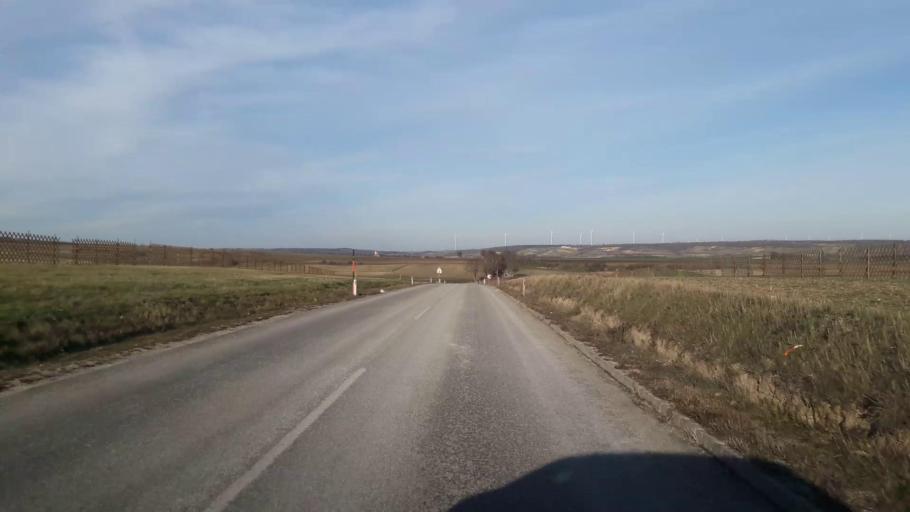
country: AT
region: Lower Austria
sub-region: Politischer Bezirk Ganserndorf
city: Auersthal
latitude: 48.3846
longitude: 16.6305
